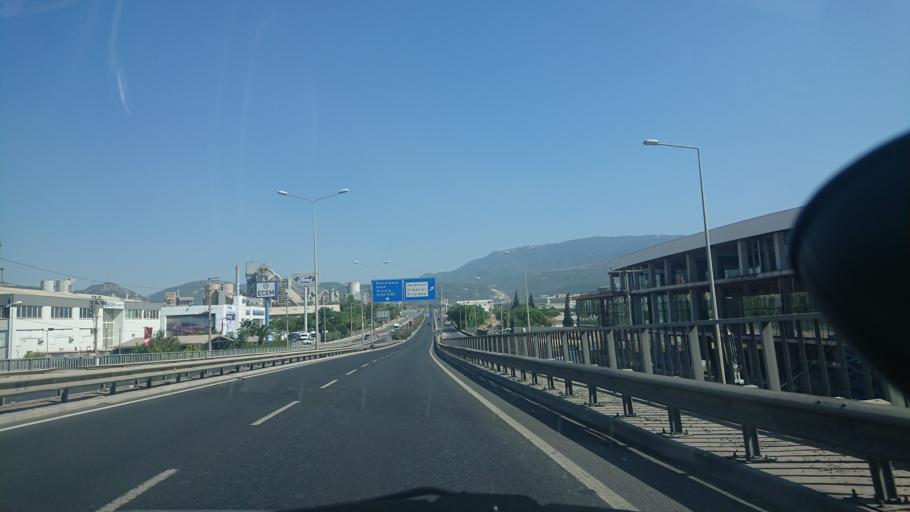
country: TR
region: Izmir
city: Bornova
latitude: 38.4569
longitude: 27.2533
